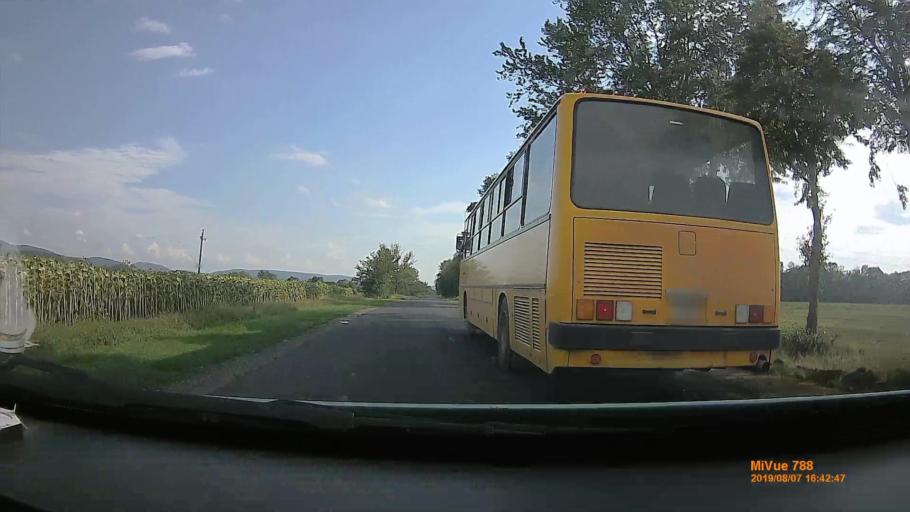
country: HU
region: Borsod-Abauj-Zemplen
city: Abaujszanto
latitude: 48.3659
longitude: 21.2158
